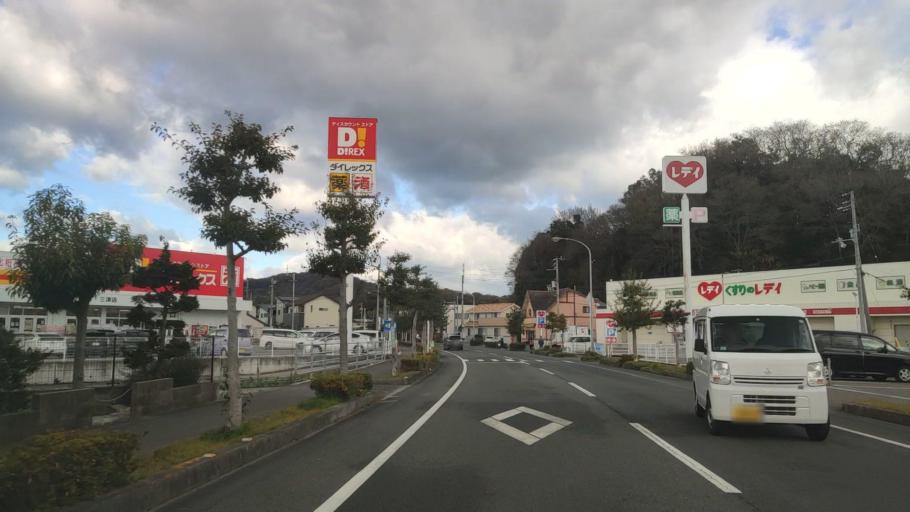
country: JP
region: Ehime
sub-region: Shikoku-chuo Shi
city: Matsuyama
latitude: 33.8677
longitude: 132.7245
